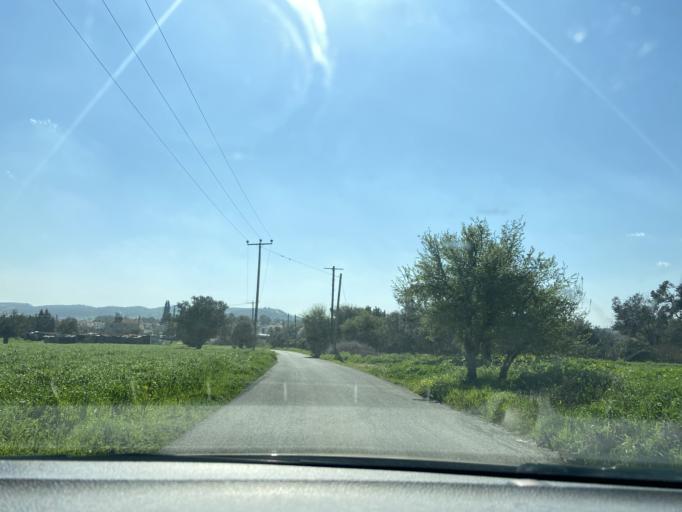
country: CY
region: Lefkosia
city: Dali
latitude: 35.0267
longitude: 33.3908
